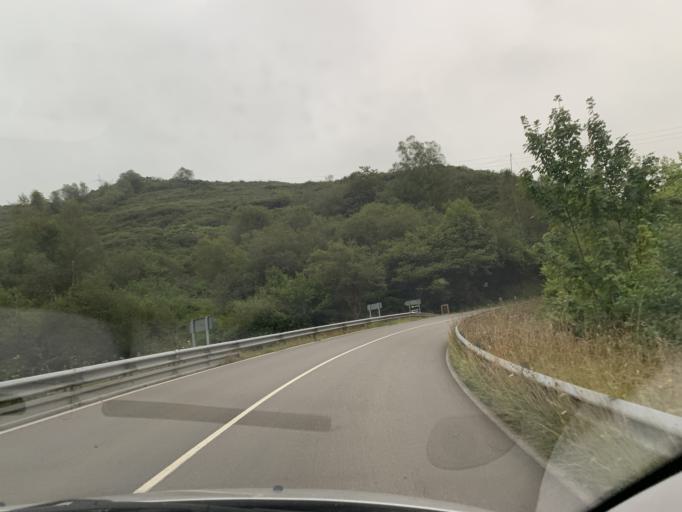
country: ES
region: Asturias
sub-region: Province of Asturias
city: Carrena
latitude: 43.3440
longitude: -4.9080
